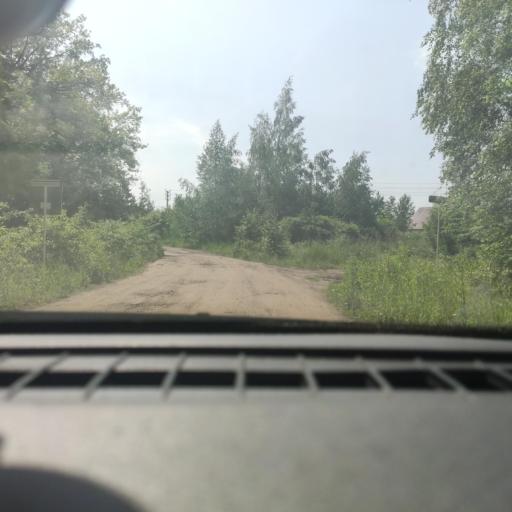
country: RU
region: Voronezj
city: Podgornoye
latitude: 51.8494
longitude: 39.2108
